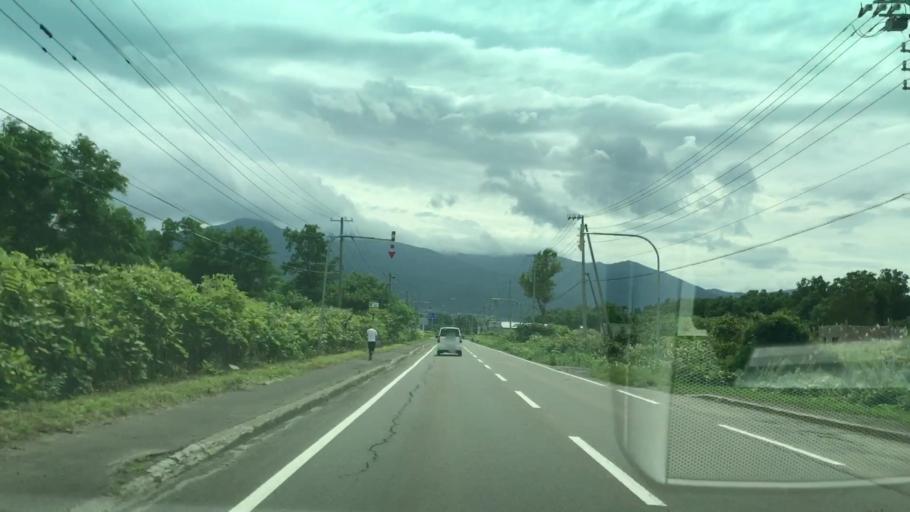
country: JP
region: Hokkaido
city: Iwanai
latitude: 43.0010
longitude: 140.5401
